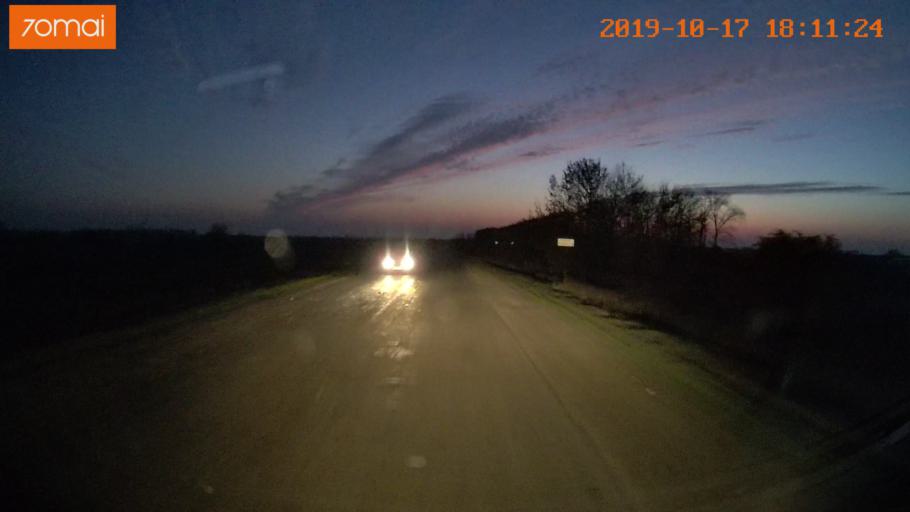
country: RU
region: Tula
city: Kurkino
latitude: 53.4157
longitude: 38.6285
